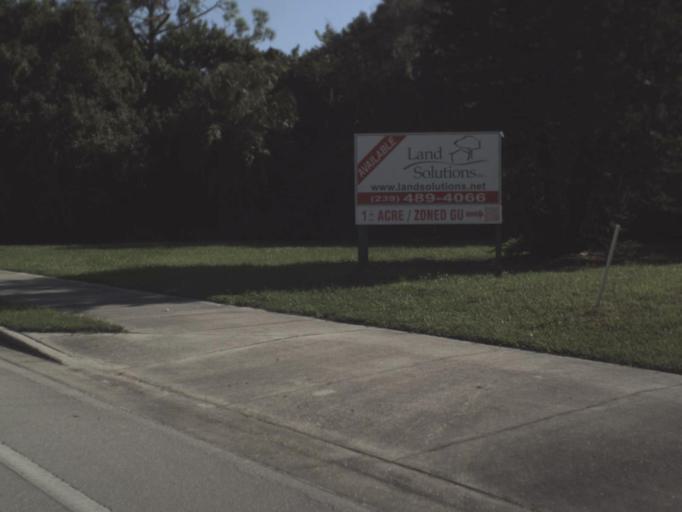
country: US
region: Florida
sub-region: Sarasota County
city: South Venice
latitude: 27.0423
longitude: -82.4012
